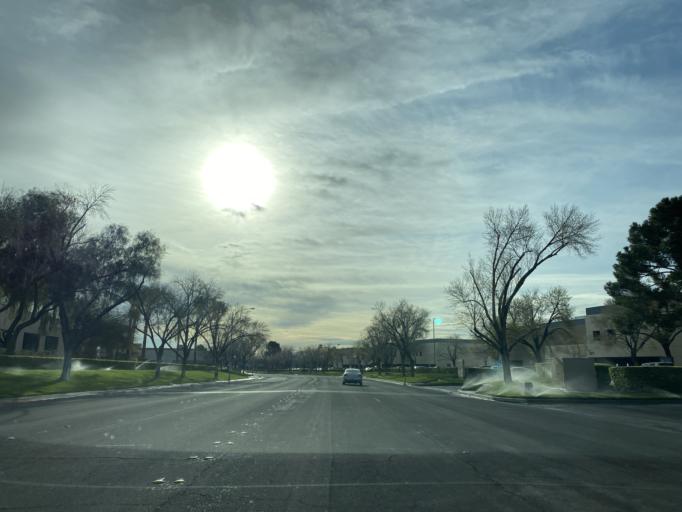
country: US
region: Nevada
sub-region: Clark County
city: Paradise
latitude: 36.0697
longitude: -115.1446
